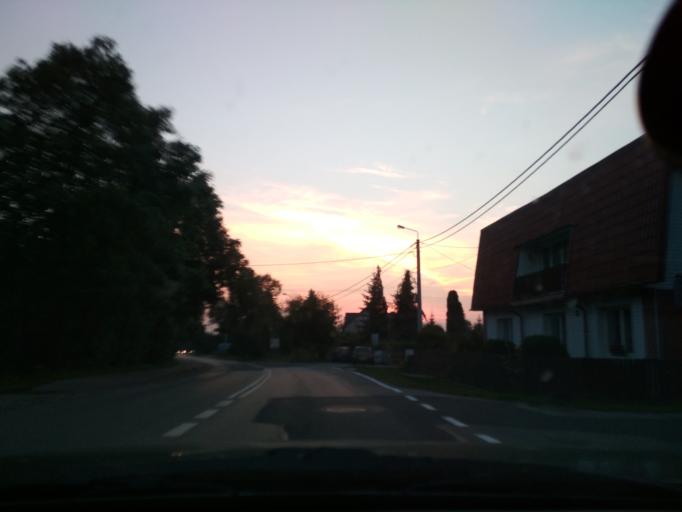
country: PL
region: Silesian Voivodeship
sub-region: Powiat zawiercianski
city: Ogrodzieniec
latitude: 50.4537
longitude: 19.5112
